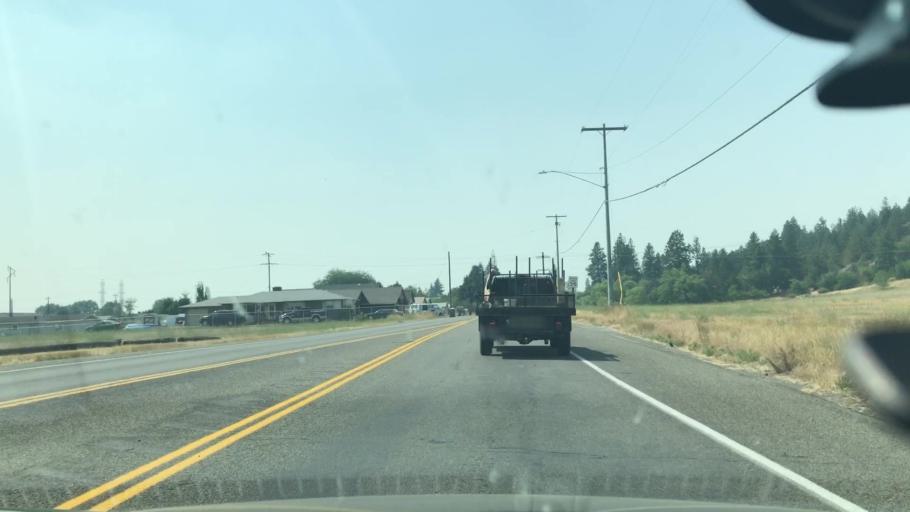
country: US
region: Washington
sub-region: Spokane County
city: Millwood
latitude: 47.6856
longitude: -117.3334
